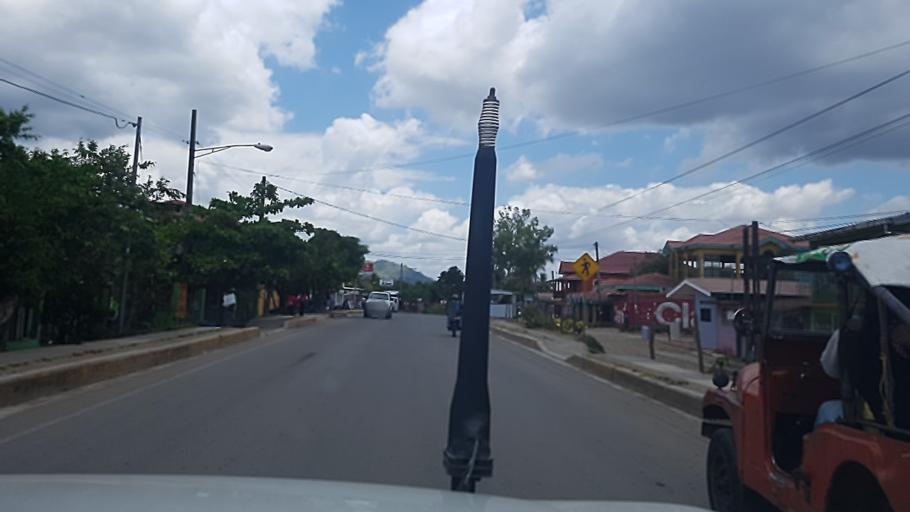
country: NI
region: Chontales
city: Santo Tomas
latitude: 12.0663
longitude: -85.0909
